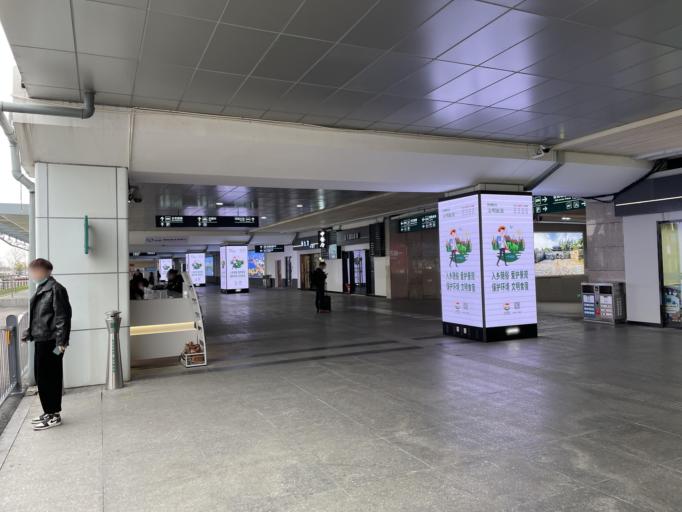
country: CN
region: Zhejiang Sheng
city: Yuxin
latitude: 30.6934
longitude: 120.7949
